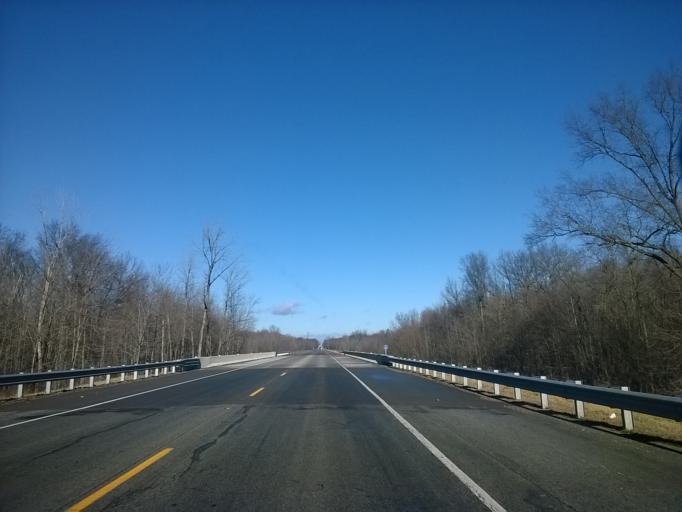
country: US
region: Indiana
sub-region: Scott County
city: Austin
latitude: 38.7622
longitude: -85.8167
